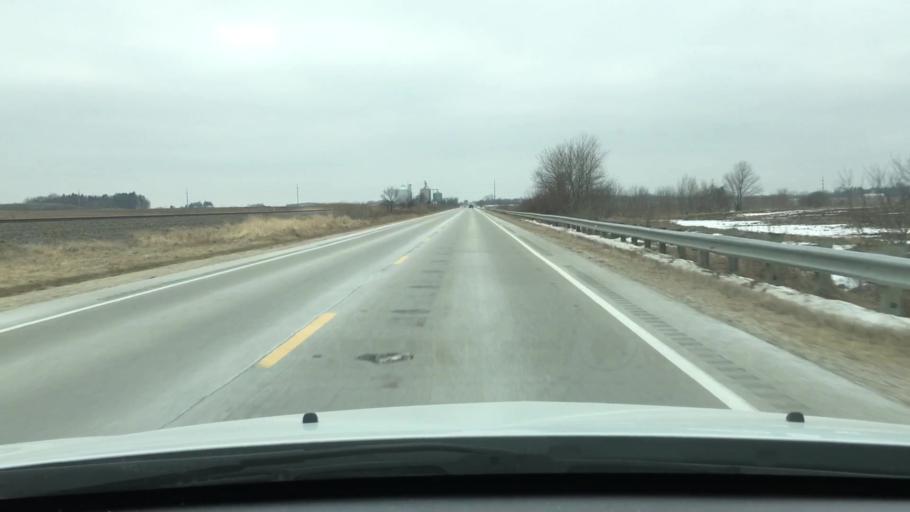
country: US
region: Illinois
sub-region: DeKalb County
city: Waterman
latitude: 41.7694
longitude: -88.7350
